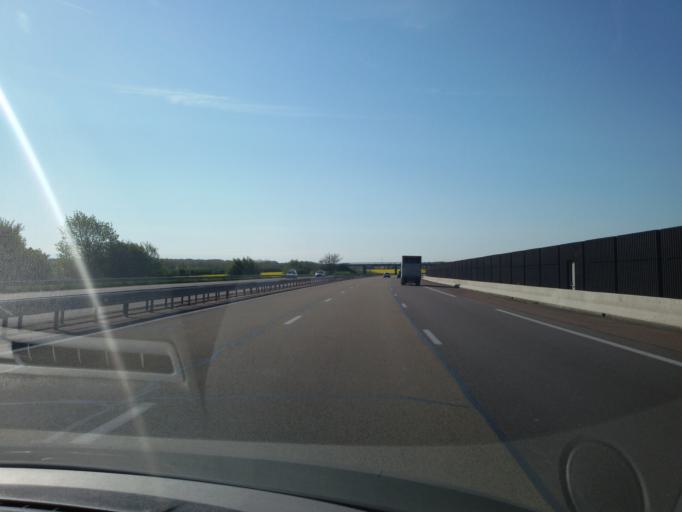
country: FR
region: Centre
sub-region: Departement du Loiret
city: Courtenay
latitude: 47.9949
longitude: 3.1757
